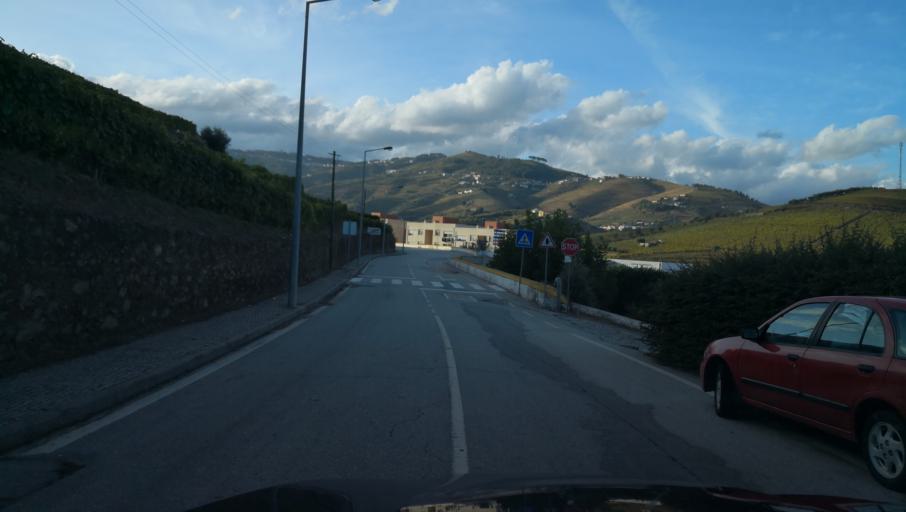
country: PT
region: Vila Real
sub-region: Santa Marta de Penaguiao
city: Santa Marta de Penaguiao
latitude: 41.2074
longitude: -7.7792
